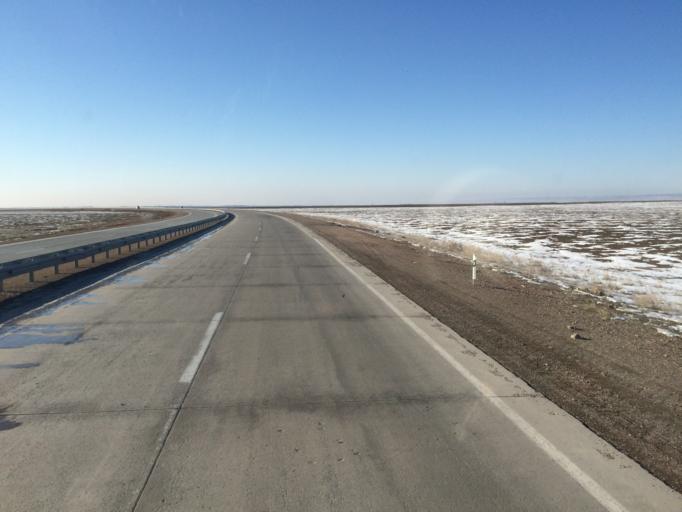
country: KG
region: Chuy
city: Sokuluk
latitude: 43.3462
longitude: 74.3004
